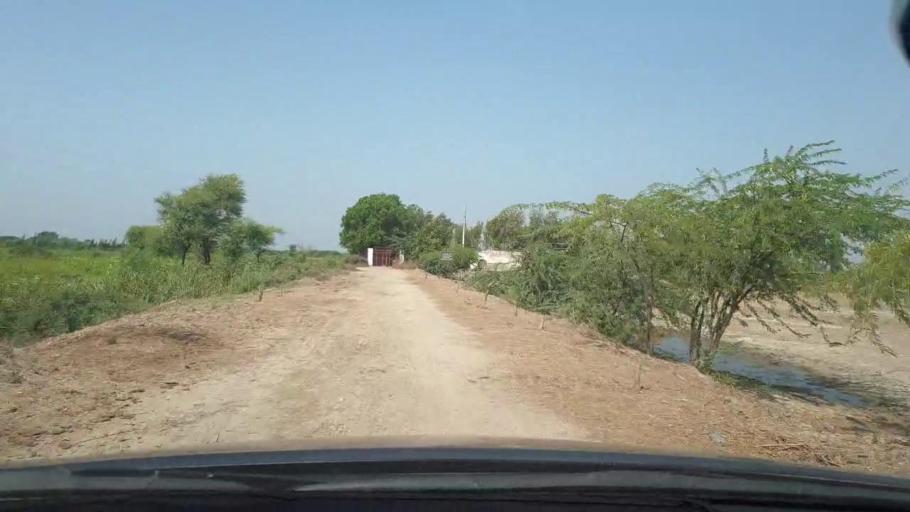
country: PK
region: Sindh
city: Tando Bago
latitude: 24.7199
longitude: 69.0962
